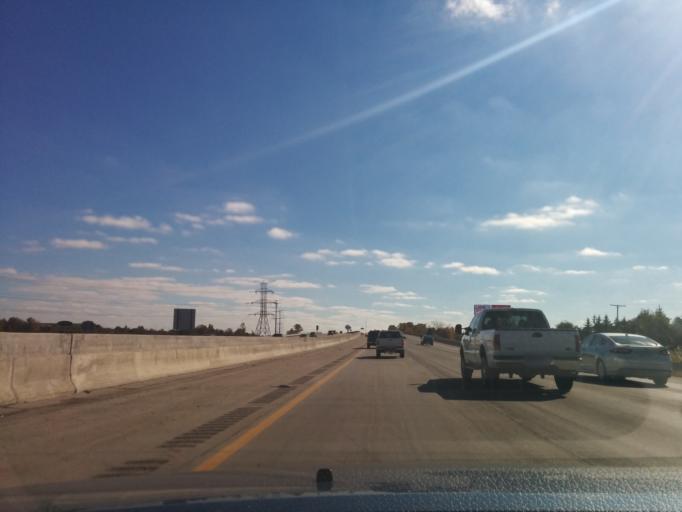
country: US
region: Michigan
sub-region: Oakland County
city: Novi
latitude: 42.4890
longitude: -83.4944
